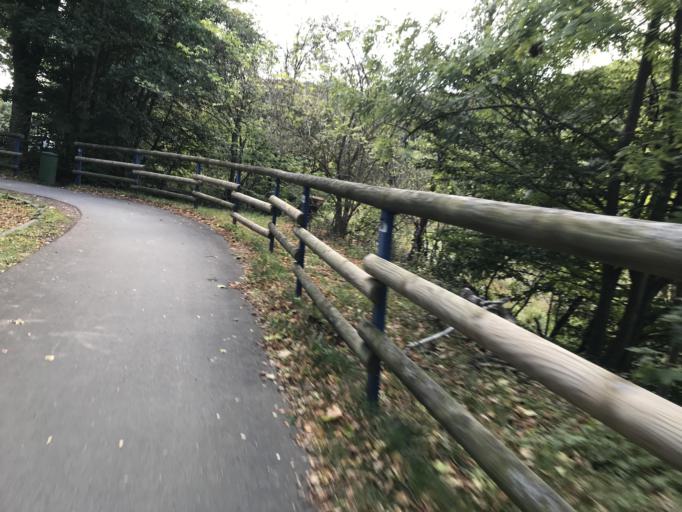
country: DE
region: Hesse
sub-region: Regierungsbezirk Kassel
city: Sachsenhausen
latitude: 51.1998
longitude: 9.0043
